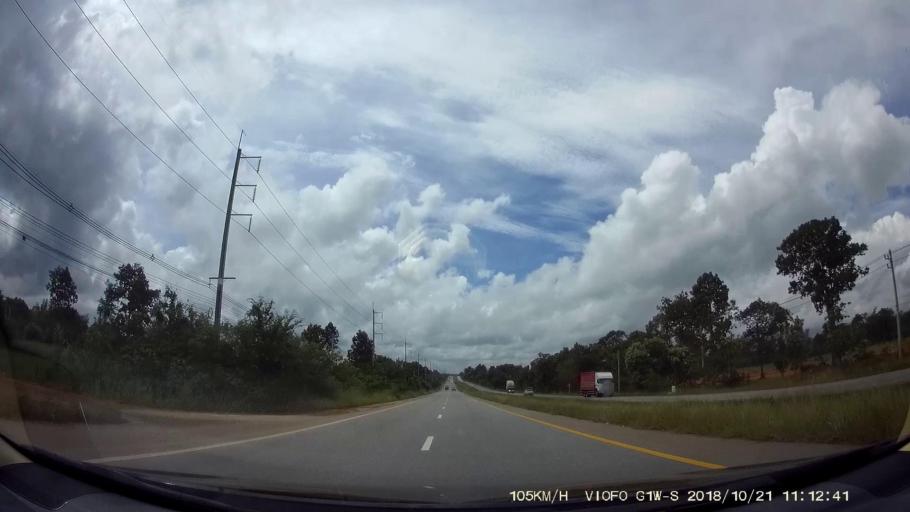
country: TH
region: Chaiyaphum
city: Khon Sawan
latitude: 15.9256
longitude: 102.1413
